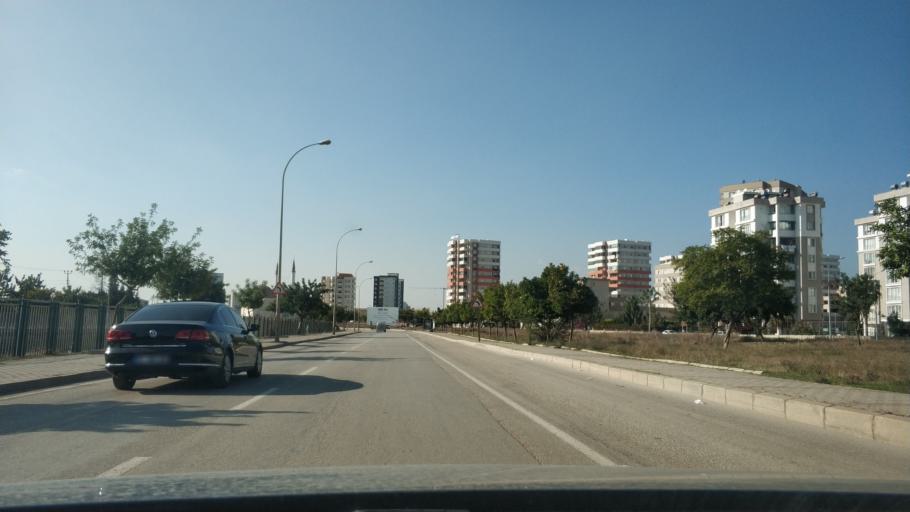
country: TR
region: Adana
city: Seyhan
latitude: 37.0096
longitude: 35.2672
